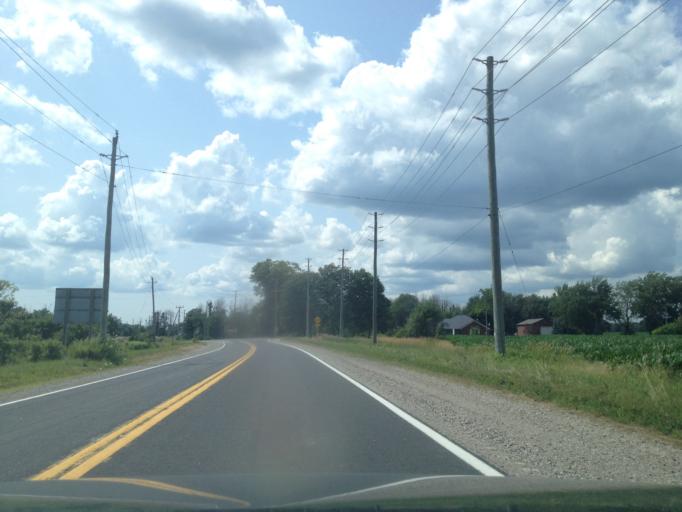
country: CA
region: Ontario
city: Aylmer
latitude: 42.6734
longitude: -80.8581
